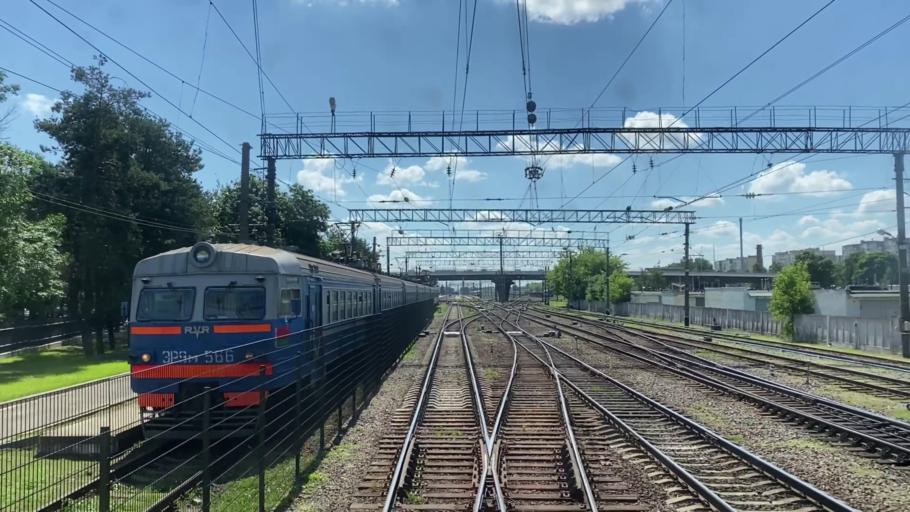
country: BY
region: Brest
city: Baranovichi
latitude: 53.1343
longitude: 26.0368
